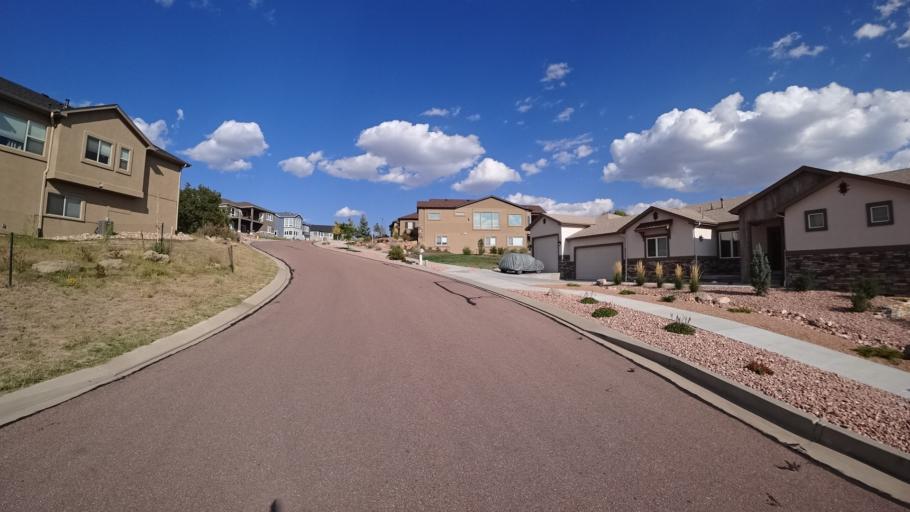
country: US
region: Colorado
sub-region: El Paso County
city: Cimarron Hills
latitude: 38.9125
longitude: -104.7411
